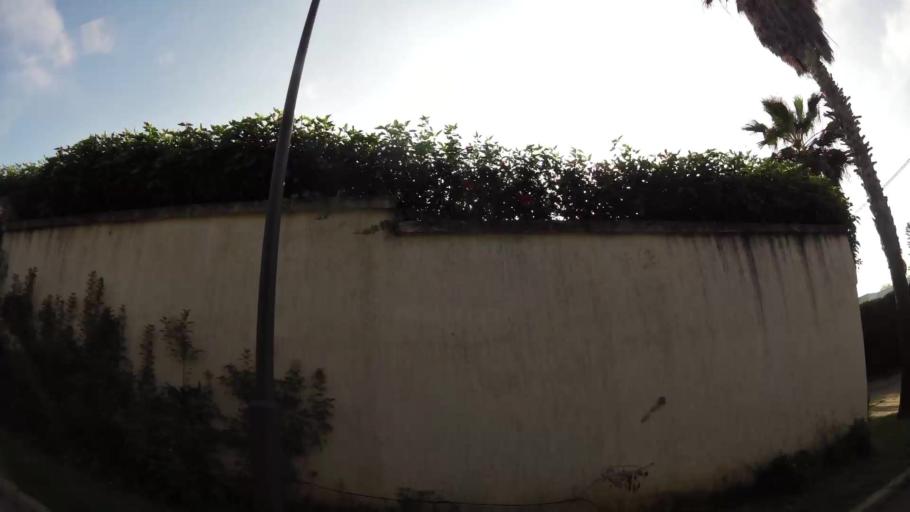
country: MA
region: Rabat-Sale-Zemmour-Zaer
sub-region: Rabat
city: Rabat
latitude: 33.9435
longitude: -6.8126
